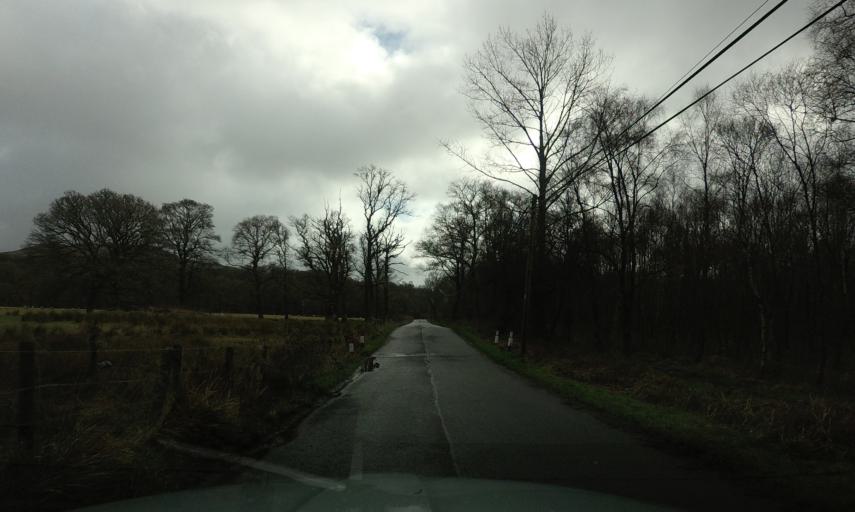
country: GB
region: Scotland
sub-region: West Dunbartonshire
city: Balloch
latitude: 56.1039
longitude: -4.5666
